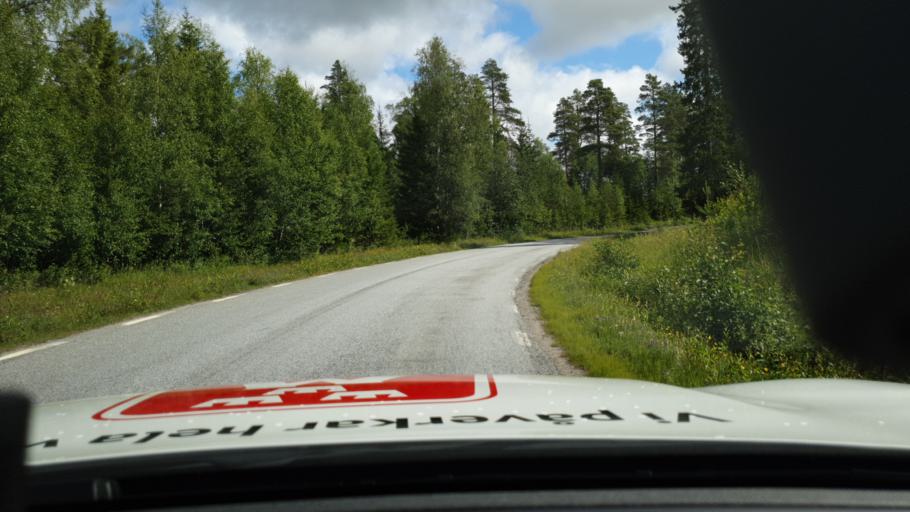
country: SE
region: Norrbotten
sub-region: Pitea Kommun
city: Rosvik
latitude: 65.4410
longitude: 21.8849
